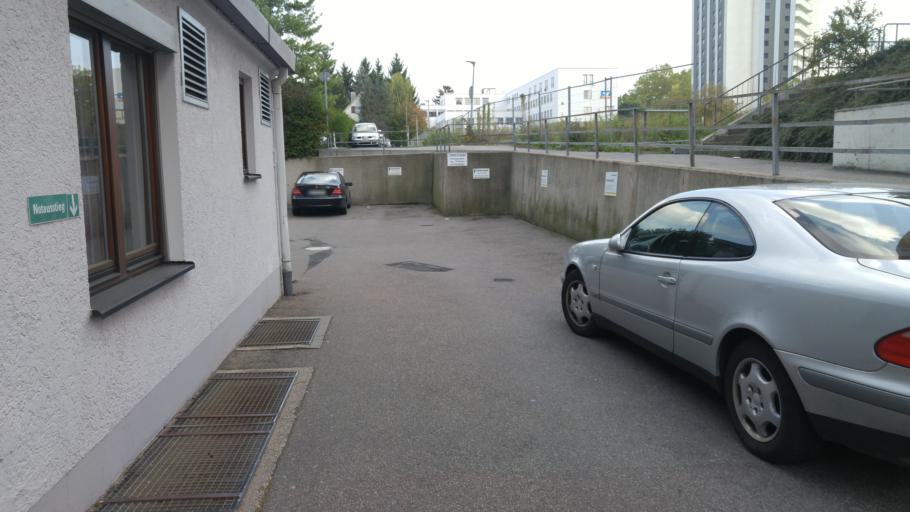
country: DE
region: Baden-Wuerttemberg
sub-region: Regierungsbezirk Stuttgart
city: Leonberg
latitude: 48.7969
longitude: 9.0124
